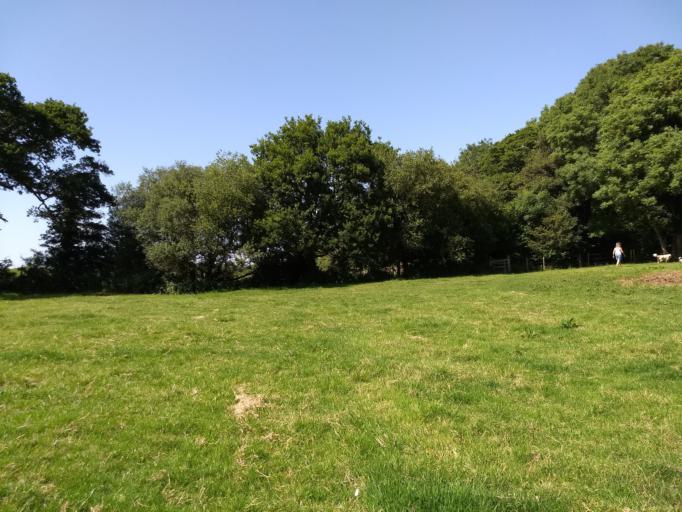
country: GB
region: England
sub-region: Isle of Wight
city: Shalfleet
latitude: 50.6940
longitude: -1.4142
